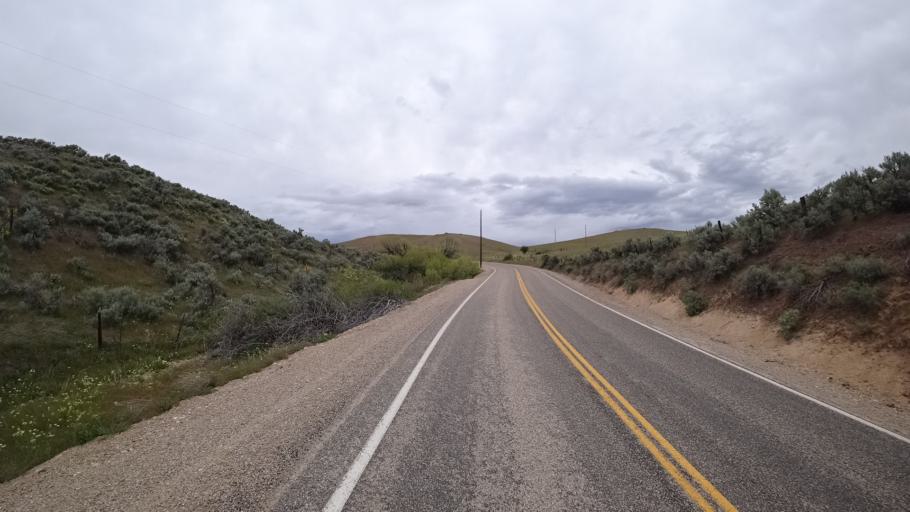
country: US
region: Idaho
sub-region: Ada County
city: Boise
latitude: 43.4863
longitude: -116.0048
